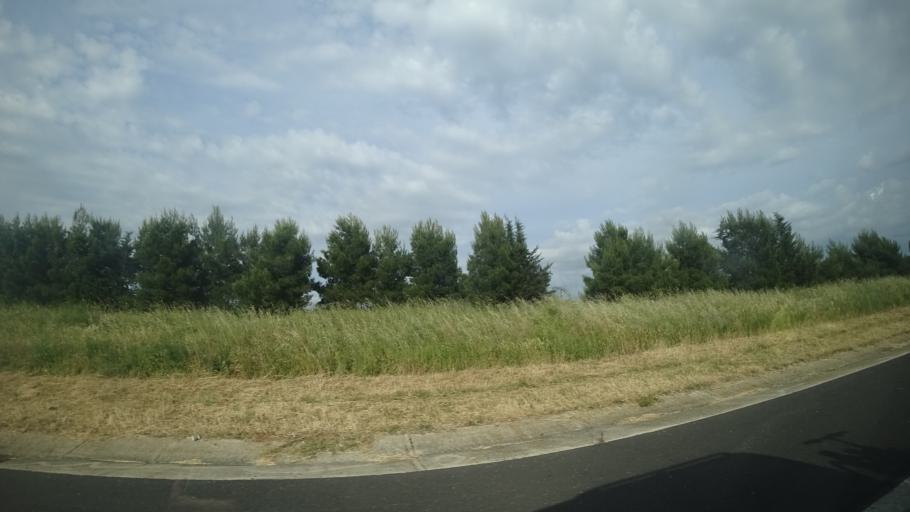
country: FR
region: Languedoc-Roussillon
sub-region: Departement de l'Herault
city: Aspiran
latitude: 43.5665
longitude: 3.4659
